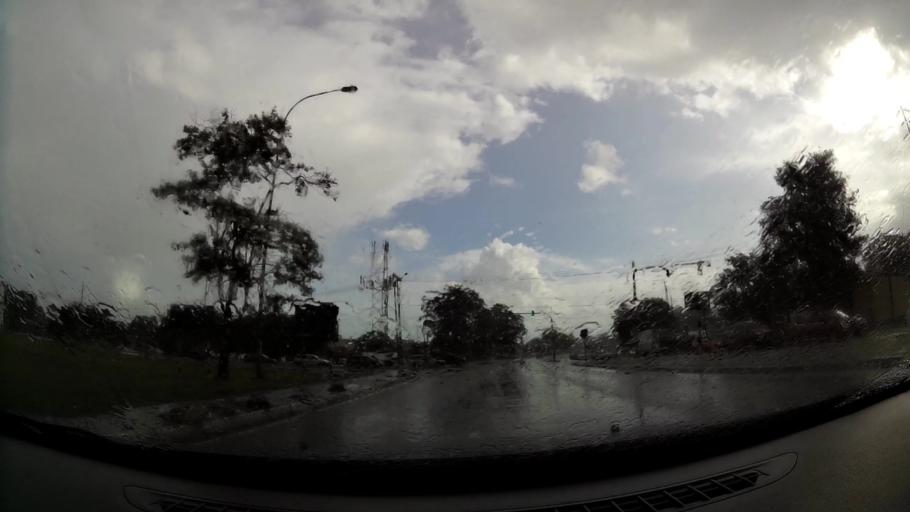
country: TT
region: Tunapuna/Piarco
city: Tunapuna
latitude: 10.6498
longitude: -61.4255
